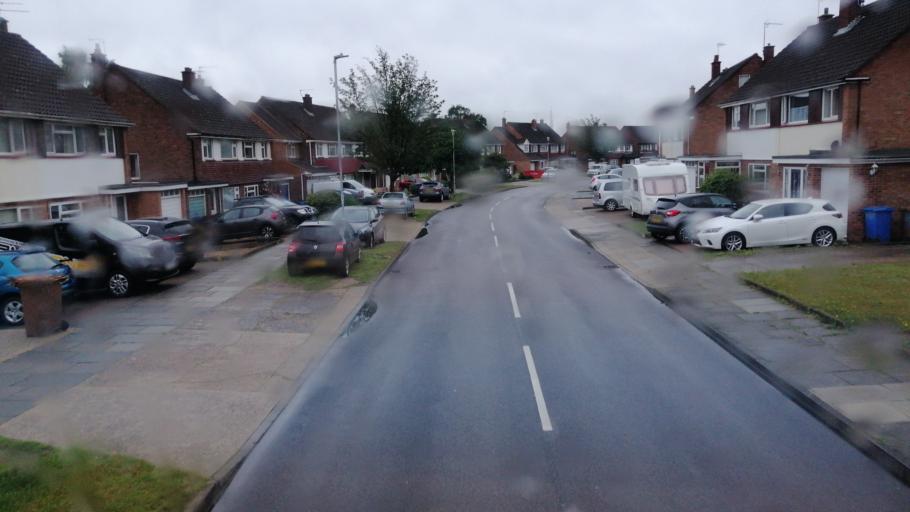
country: GB
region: England
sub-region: Suffolk
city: Kesgrave
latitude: 52.0443
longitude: 1.2036
